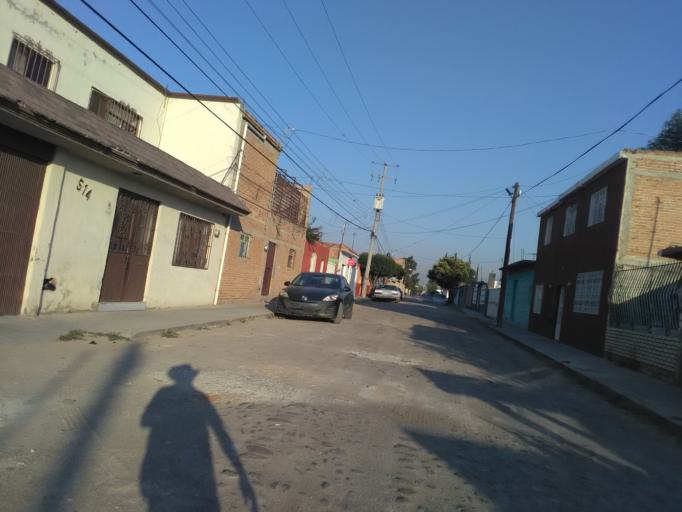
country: MX
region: Durango
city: Victoria de Durango
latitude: 24.0386
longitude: -104.6423
